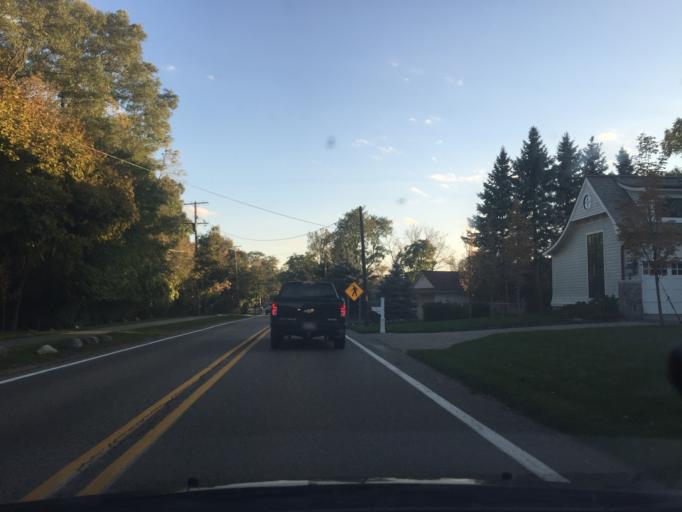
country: US
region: Michigan
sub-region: Oakland County
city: Bloomfield Hills
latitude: 42.5878
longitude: -83.2868
